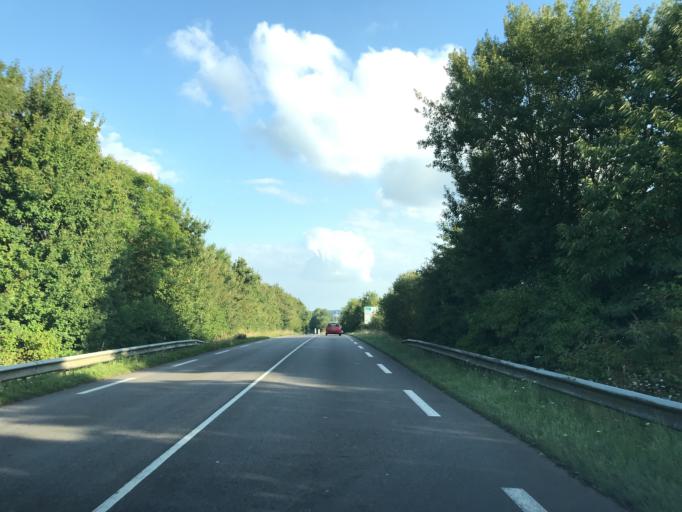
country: FR
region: Haute-Normandie
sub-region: Departement de la Seine-Maritime
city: Bolbec
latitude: 49.5769
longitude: 0.4546
